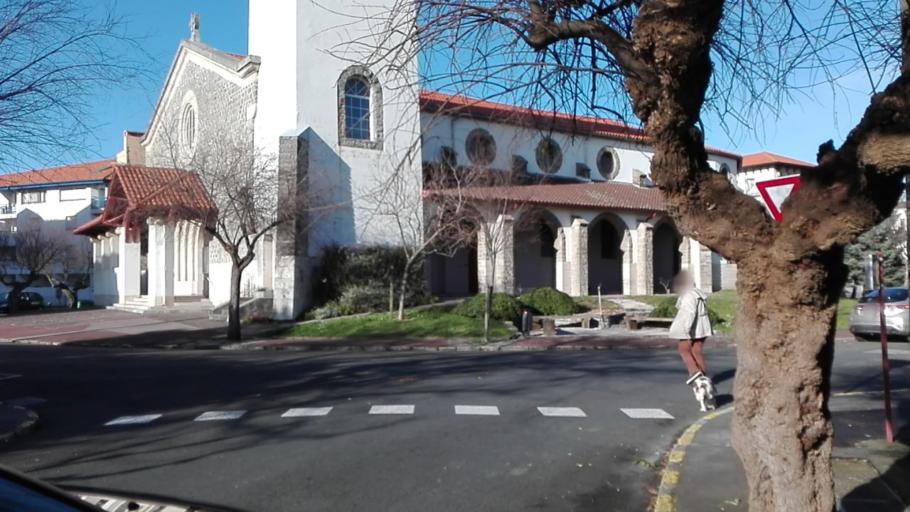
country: FR
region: Aquitaine
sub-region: Departement des Pyrenees-Atlantiques
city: Hendaye
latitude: 43.3731
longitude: -1.7695
